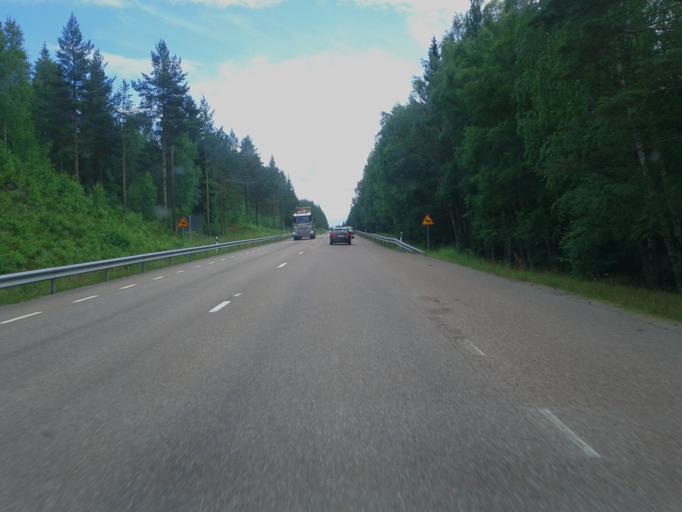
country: SE
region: Dalarna
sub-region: Faluns Kommun
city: Bjursas
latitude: 60.7135
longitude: 15.4610
